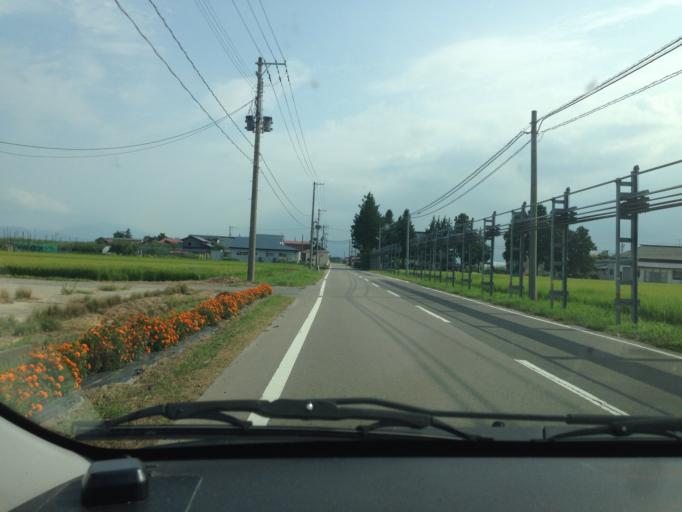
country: JP
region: Fukushima
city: Kitakata
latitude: 37.5687
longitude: 139.8534
